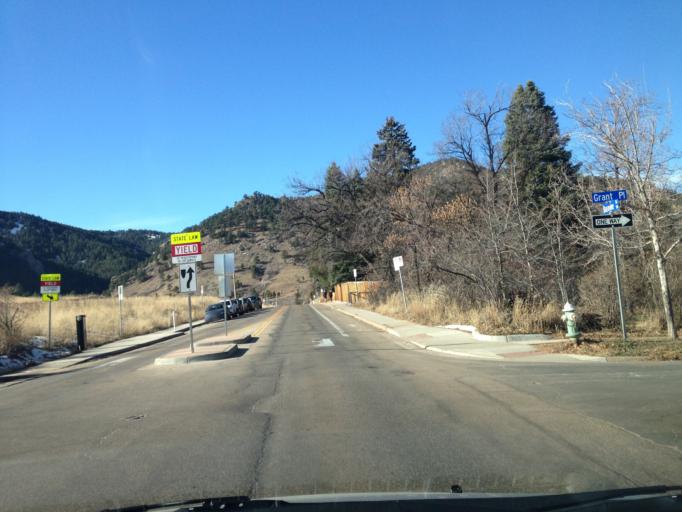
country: US
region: Colorado
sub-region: Boulder County
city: Boulder
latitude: 40.0001
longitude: -105.2828
